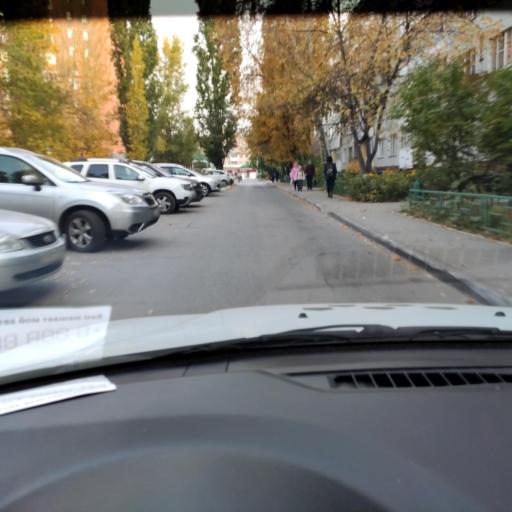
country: RU
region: Samara
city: Tol'yatti
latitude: 53.5087
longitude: 49.4368
